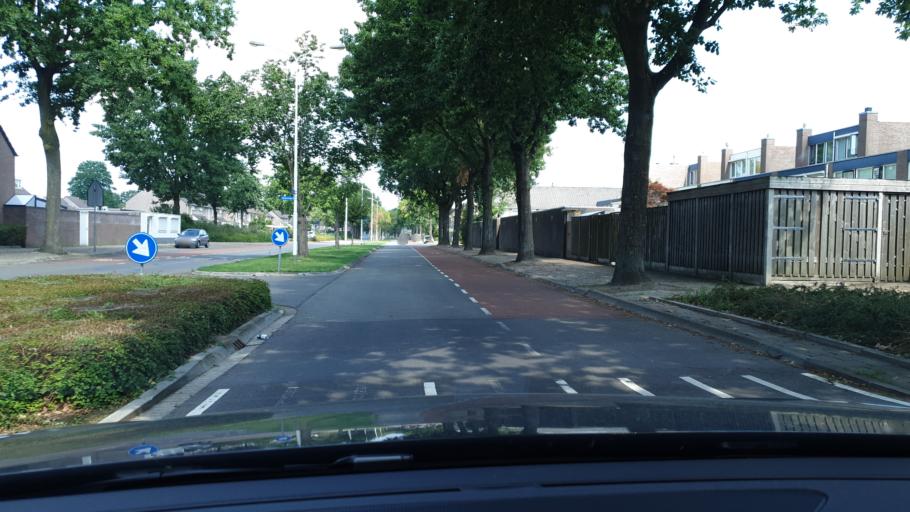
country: NL
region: North Brabant
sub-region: Gemeente Son en Breugel
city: Son
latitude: 51.4870
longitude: 5.4494
